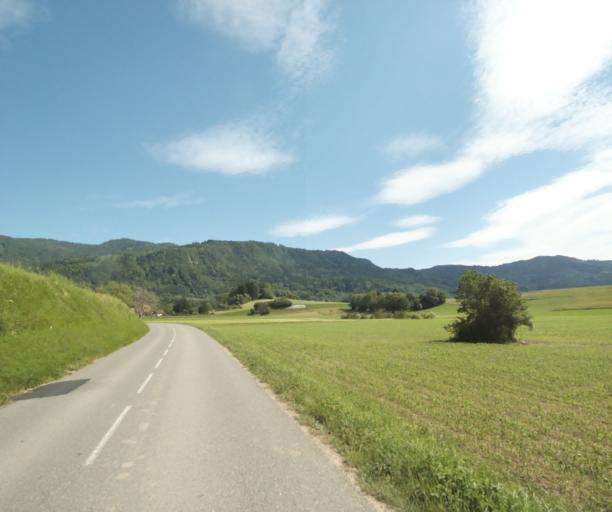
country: FR
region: Rhone-Alpes
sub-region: Departement de la Haute-Savoie
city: Perrignier
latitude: 46.2998
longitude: 6.4496
